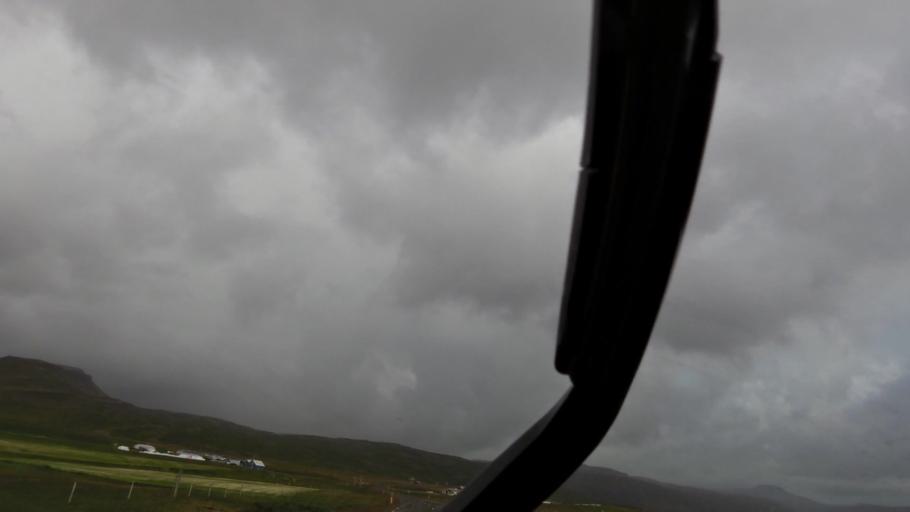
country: IS
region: Westfjords
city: Isafjoerdur
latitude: 65.5231
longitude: -23.1888
